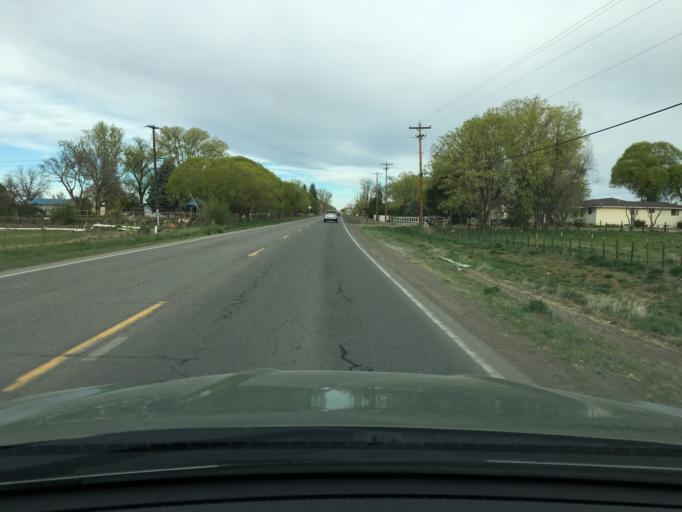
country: US
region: Colorado
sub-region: Delta County
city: Paonia
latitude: 38.7998
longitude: -107.7480
